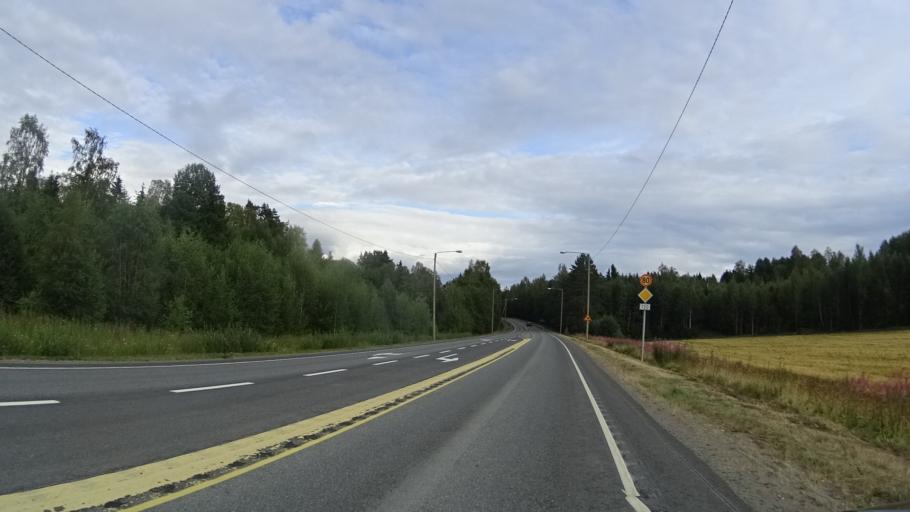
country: FI
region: Haeme
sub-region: Haemeenlinna
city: Parola
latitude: 61.0287
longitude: 24.2809
